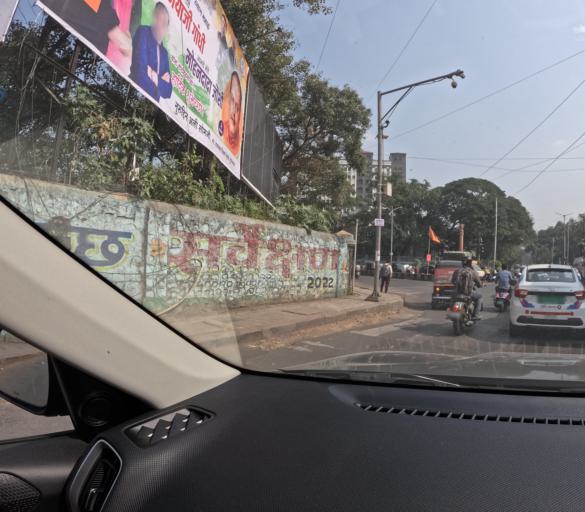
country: IN
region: Maharashtra
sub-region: Pune Division
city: Pune
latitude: 18.5257
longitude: 73.8673
